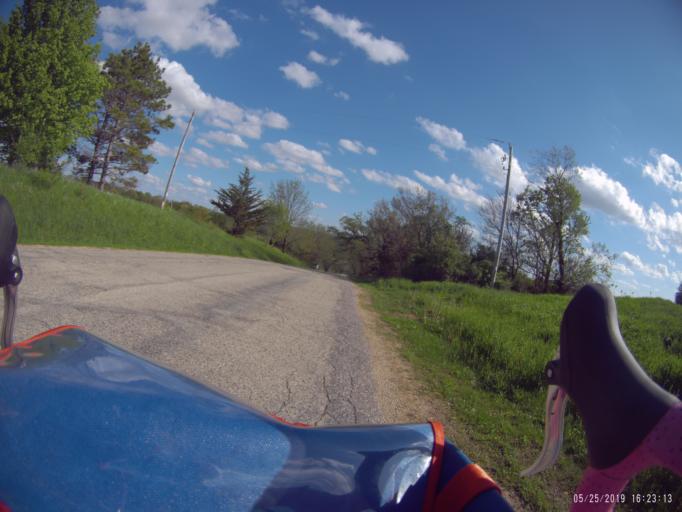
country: US
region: Wisconsin
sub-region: Dane County
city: Mount Horeb
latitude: 42.9594
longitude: -89.7014
